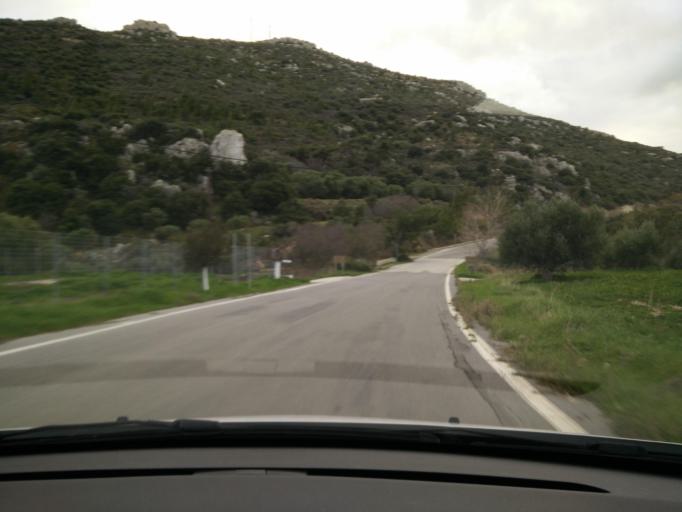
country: GR
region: Crete
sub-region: Nomos Lasithiou
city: Gra Liyia
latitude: 35.0816
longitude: 25.7106
